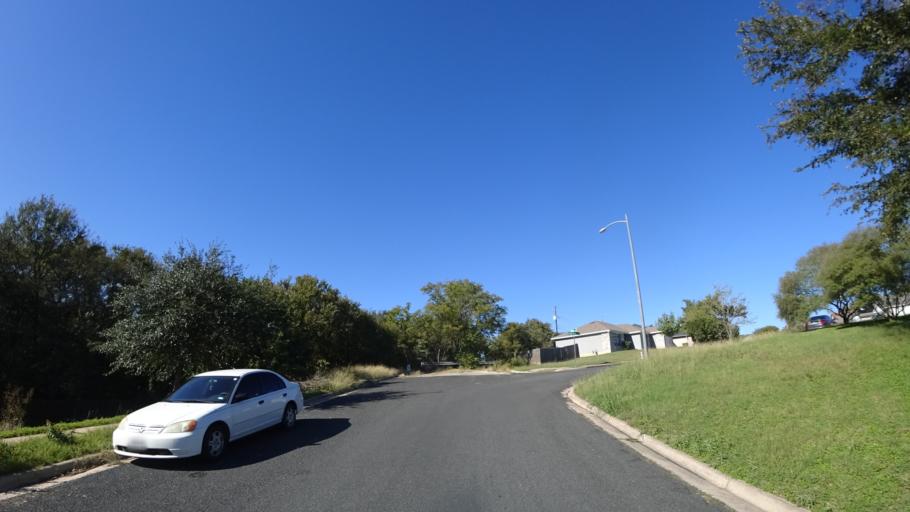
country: US
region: Texas
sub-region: Travis County
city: Austin
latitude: 30.2911
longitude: -97.6777
